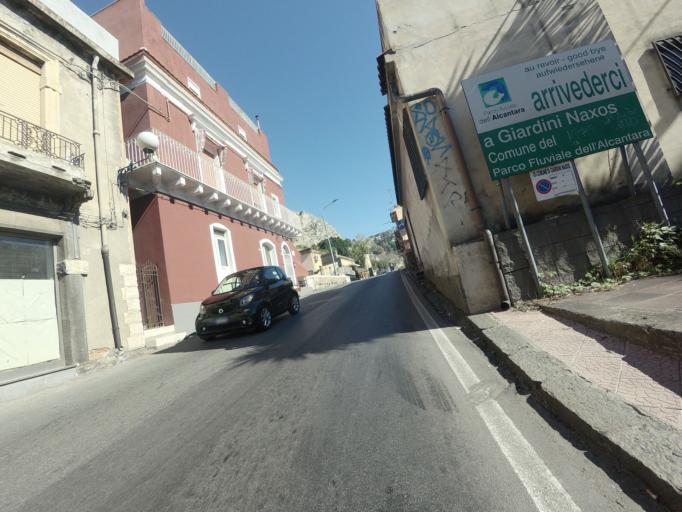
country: IT
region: Sicily
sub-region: Messina
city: Taormina
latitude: 37.8432
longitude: 15.2797
